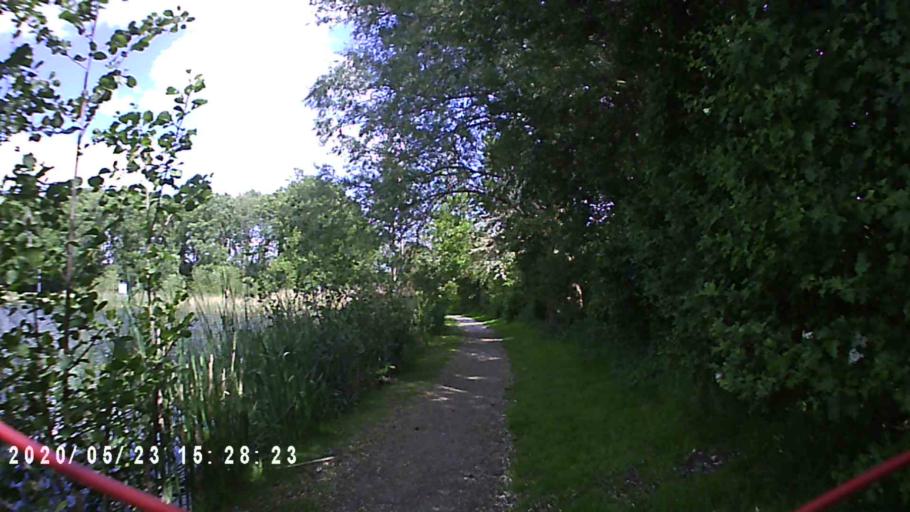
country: NL
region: Groningen
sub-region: Gemeente Delfzijl
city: Delfzijl
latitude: 53.2562
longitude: 6.9261
